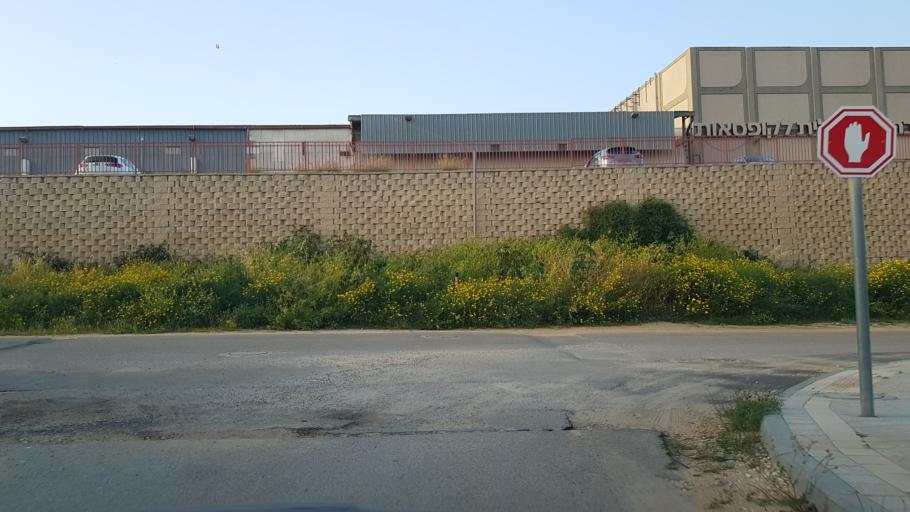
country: IL
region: Central District
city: Ra'anana
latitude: 32.1977
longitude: 34.8886
